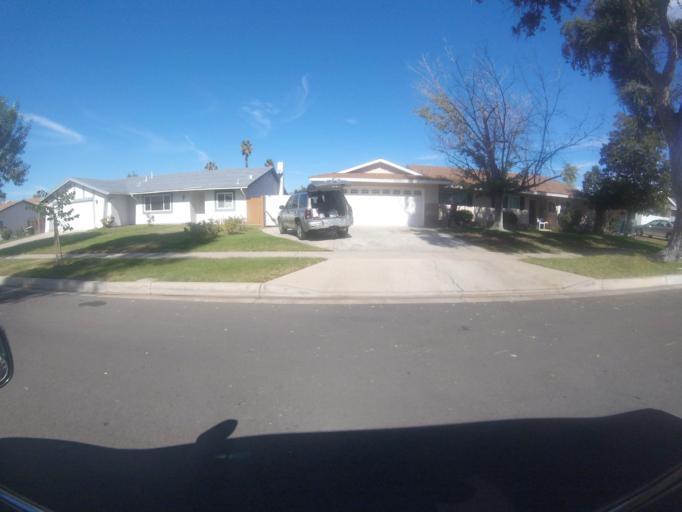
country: US
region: California
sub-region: San Bernardino County
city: Mentone
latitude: 34.0636
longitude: -117.1531
